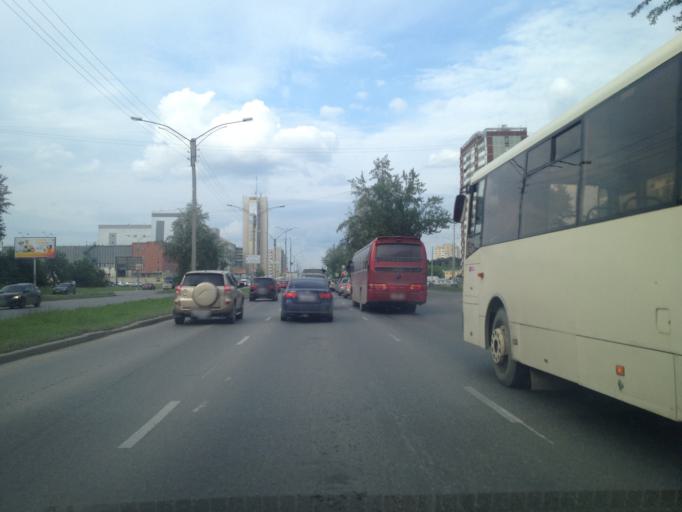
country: RU
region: Sverdlovsk
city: Sovkhoznyy
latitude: 56.8088
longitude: 60.5449
